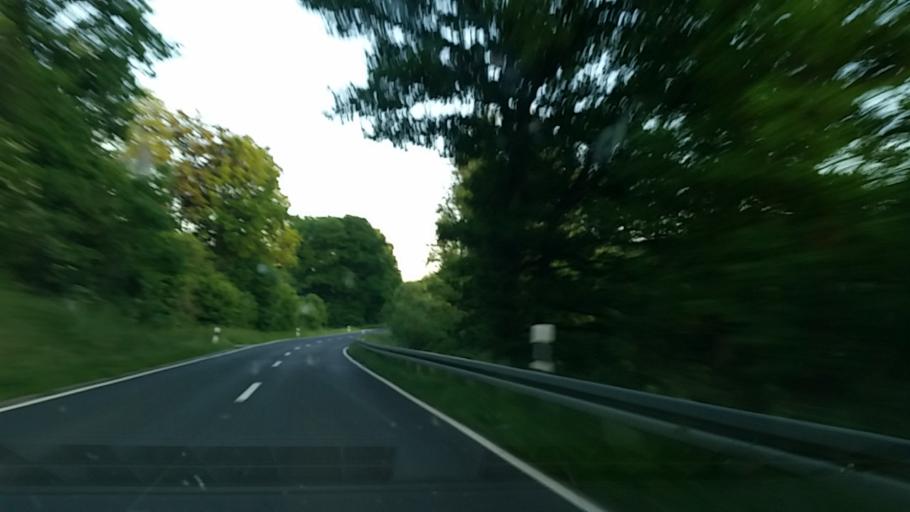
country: DE
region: Bavaria
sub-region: Regierungsbezirk Unterfranken
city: Mittelsinn
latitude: 50.1756
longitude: 9.6396
